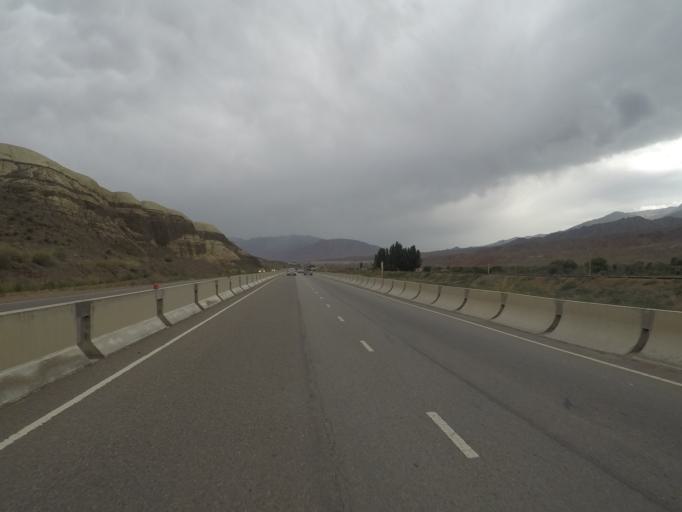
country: KG
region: Chuy
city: Bystrovka
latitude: 42.5247
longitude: 75.8238
